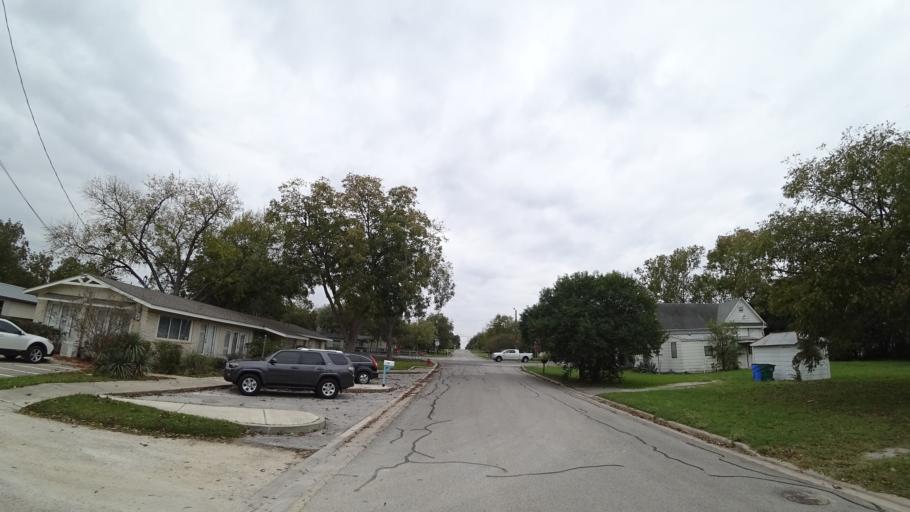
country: US
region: Texas
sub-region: Travis County
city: Pflugerville
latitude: 30.4411
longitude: -97.6223
